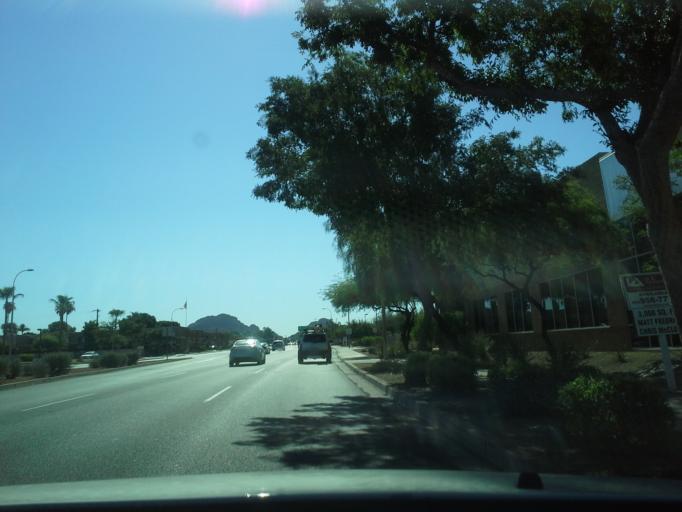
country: US
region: Arizona
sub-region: Maricopa County
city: Tempe Junction
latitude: 33.4656
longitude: -111.9861
